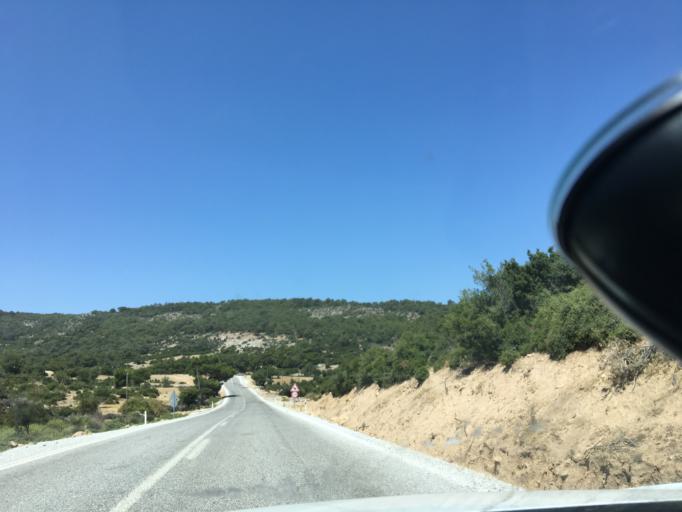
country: TR
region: Canakkale
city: Gulpinar
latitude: 39.4889
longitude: 26.1555
